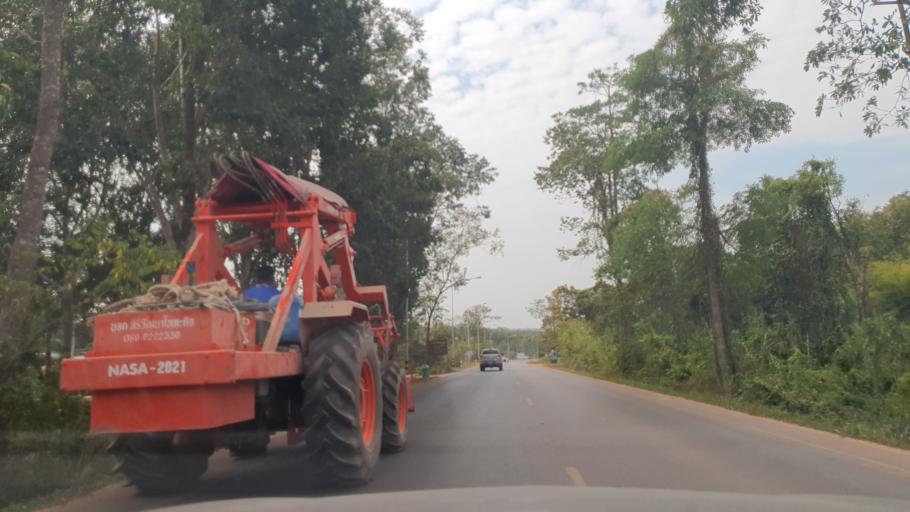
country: TH
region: Changwat Bueng Kan
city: Si Wilai
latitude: 18.2724
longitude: 103.8419
